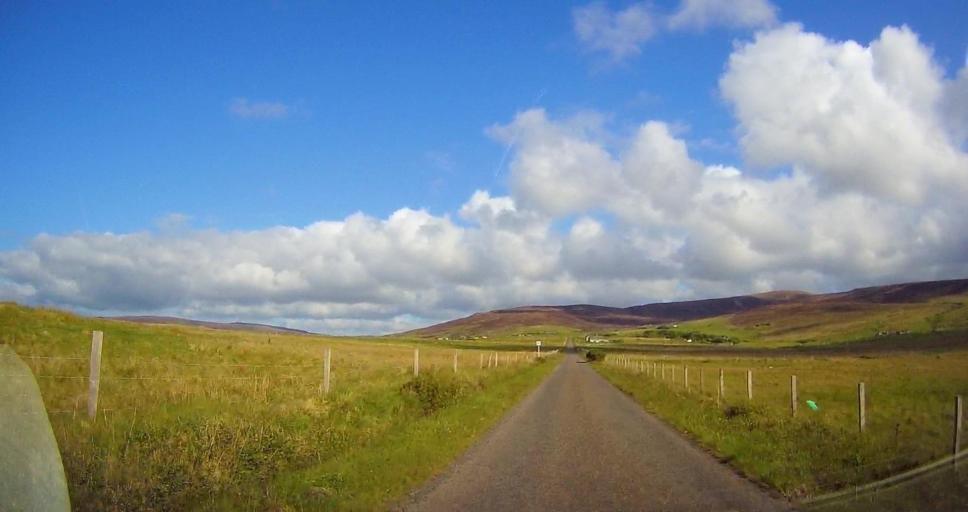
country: GB
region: Scotland
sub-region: Orkney Islands
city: Stromness
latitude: 58.9826
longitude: -3.1827
